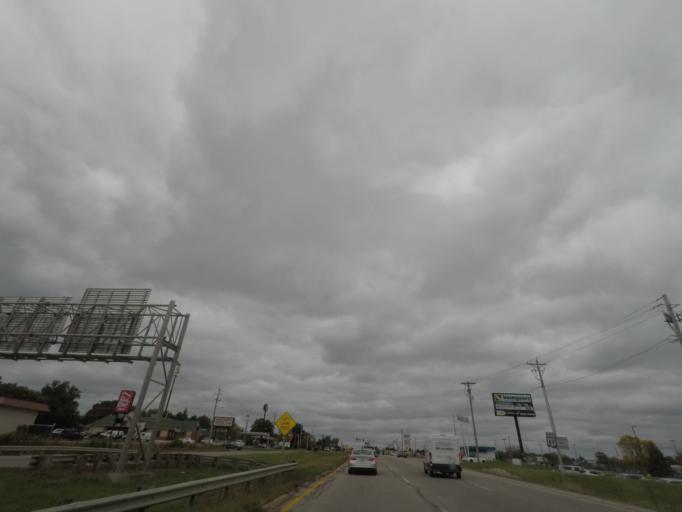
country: US
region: Iowa
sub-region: Polk County
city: Saylorville
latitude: 41.6515
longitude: -93.6003
